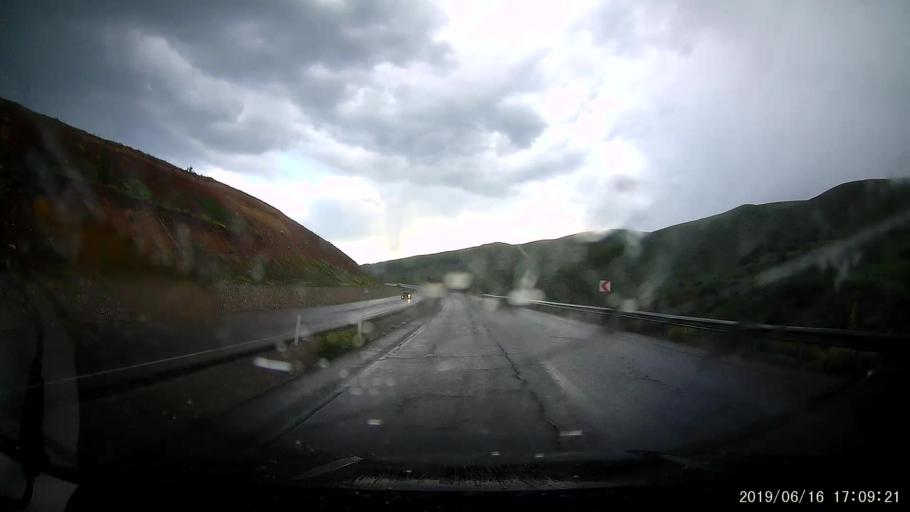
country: TR
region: Erzurum
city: Askale
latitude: 39.8964
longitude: 40.6502
